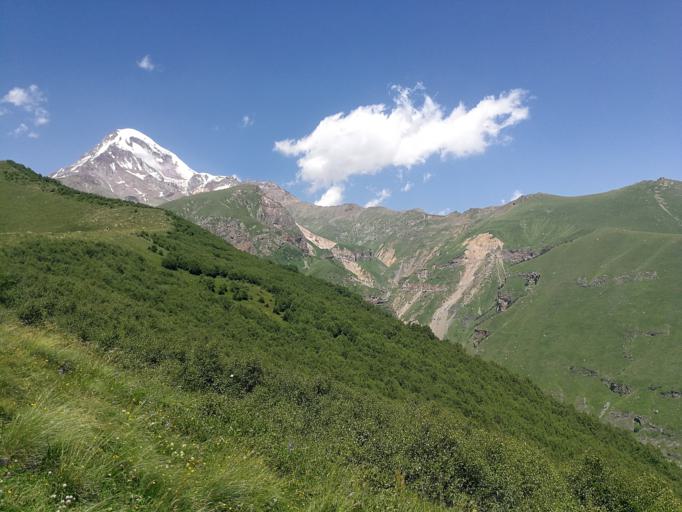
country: GE
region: Mtskheta-Mtianeti
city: Step'antsminda
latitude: 42.6649
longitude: 44.6110
